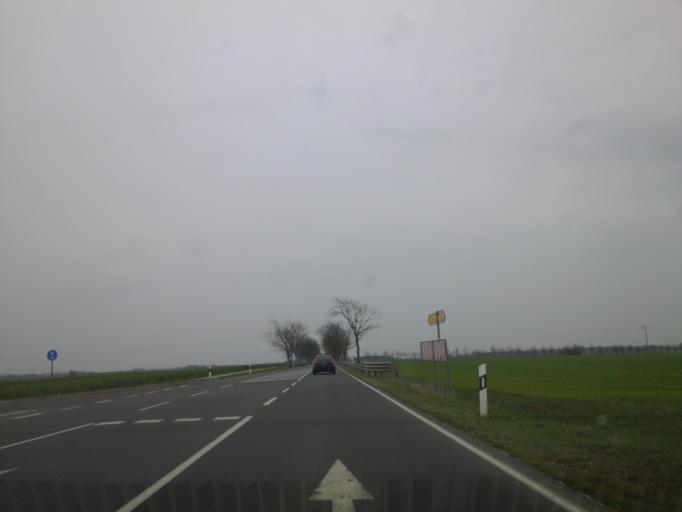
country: DE
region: Mecklenburg-Vorpommern
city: Barth
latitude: 54.3277
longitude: 12.7212
